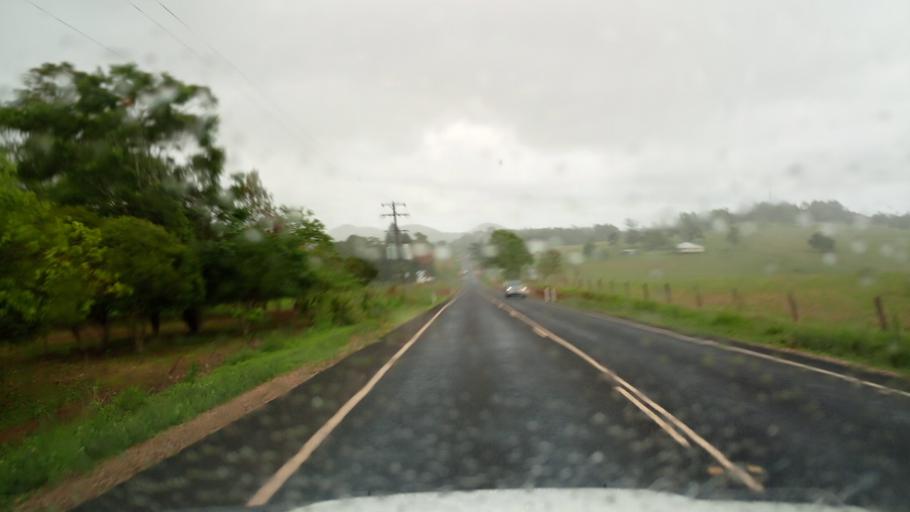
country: AU
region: Queensland
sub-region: Tablelands
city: Atherton
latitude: -17.2798
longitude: 145.5926
